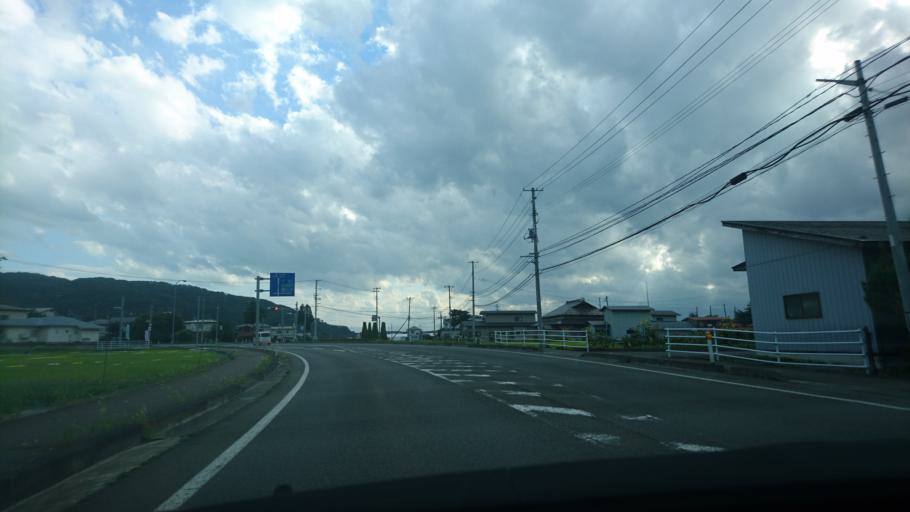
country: JP
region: Iwate
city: Kitakami
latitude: 39.2848
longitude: 141.1373
